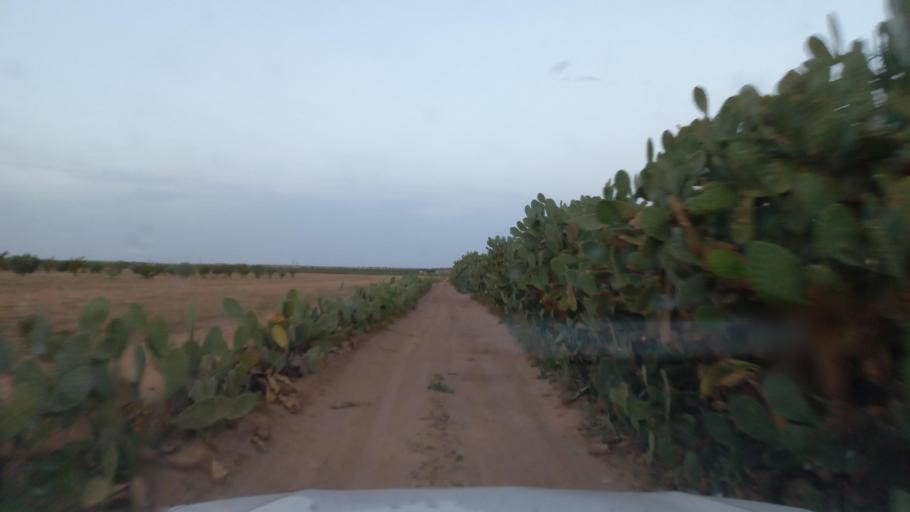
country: TN
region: Al Qasrayn
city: Sbiba
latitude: 35.3517
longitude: 9.0418
